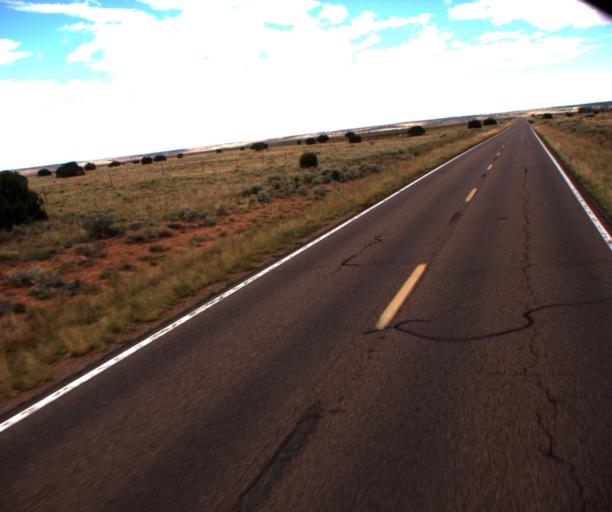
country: US
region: Arizona
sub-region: Navajo County
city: Heber-Overgaard
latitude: 34.6003
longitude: -110.3880
